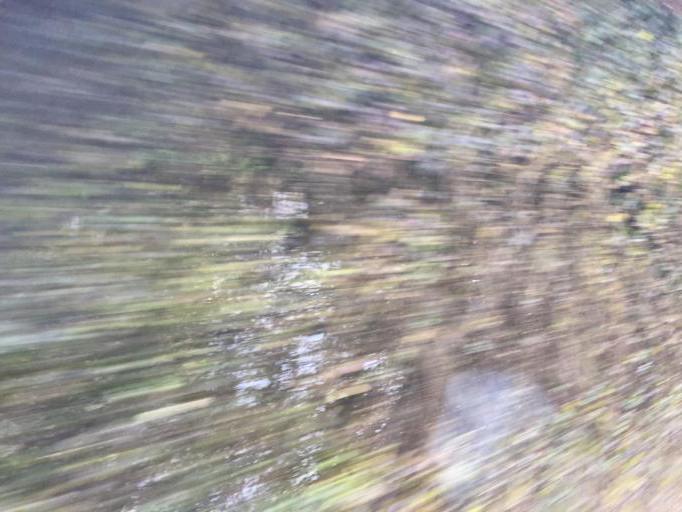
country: GB
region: Wales
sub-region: Monmouthshire
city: Caldicot
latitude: 51.5984
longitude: -2.7101
